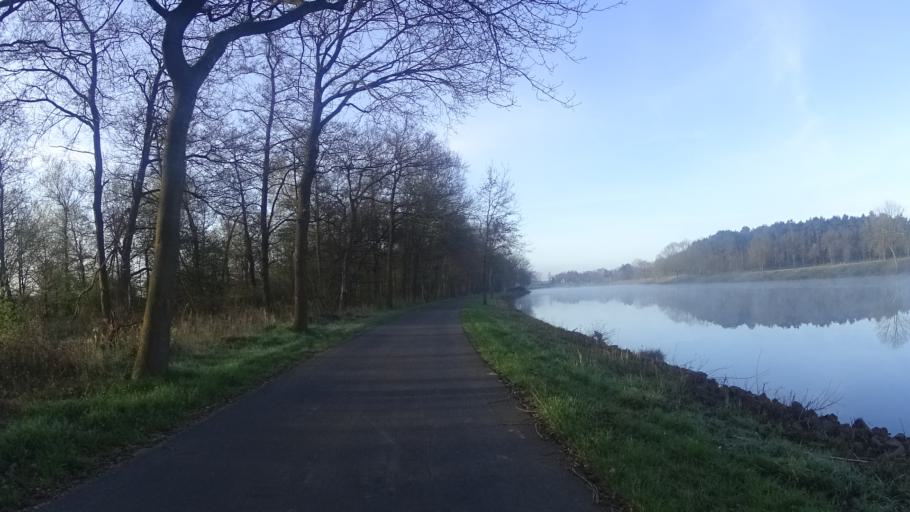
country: DE
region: Lower Saxony
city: Fresenburg
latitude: 52.9102
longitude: 7.3138
